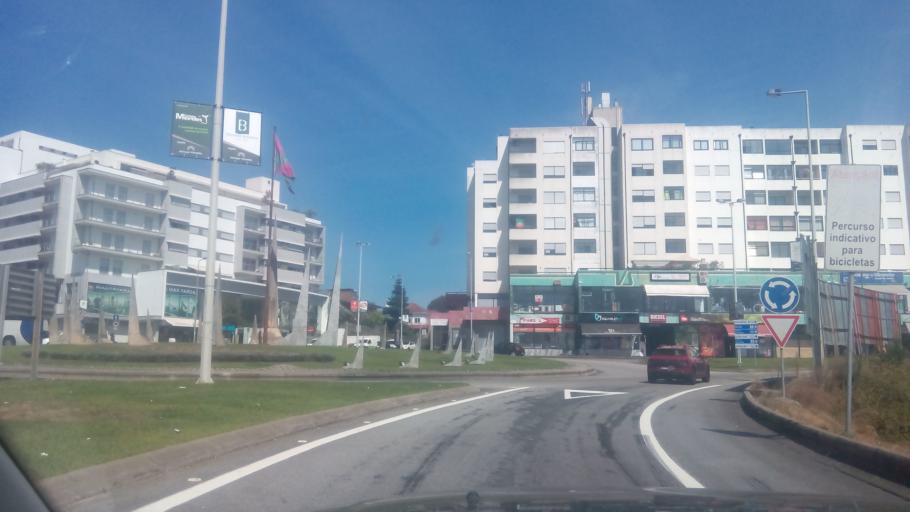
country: PT
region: Porto
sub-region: Paredes
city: Casteloes de Cepeda
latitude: 41.2057
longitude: -8.3358
